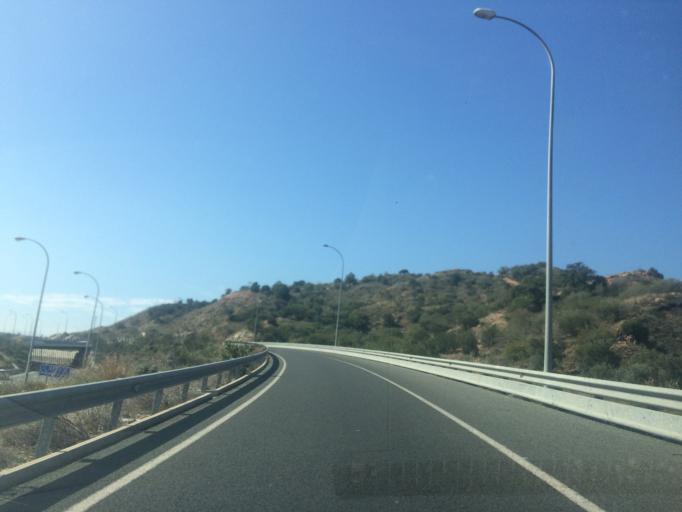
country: ES
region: Andalusia
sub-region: Provincia de Malaga
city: Malaga
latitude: 36.7470
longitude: -4.4407
